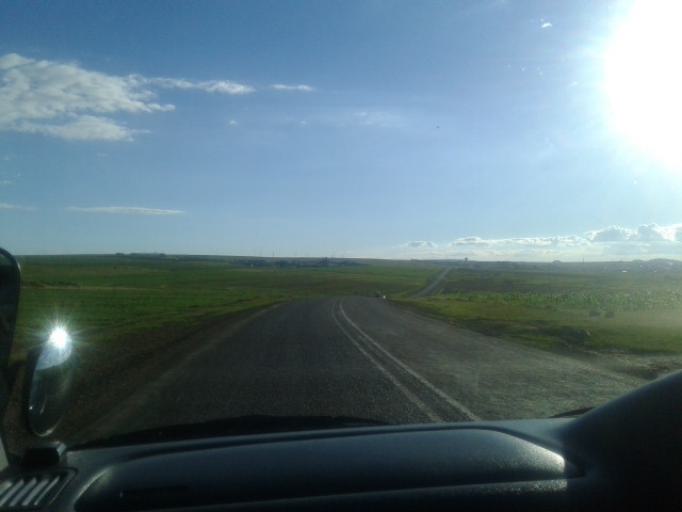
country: LS
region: Maseru
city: Maseru
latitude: -29.3025
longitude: 27.6110
